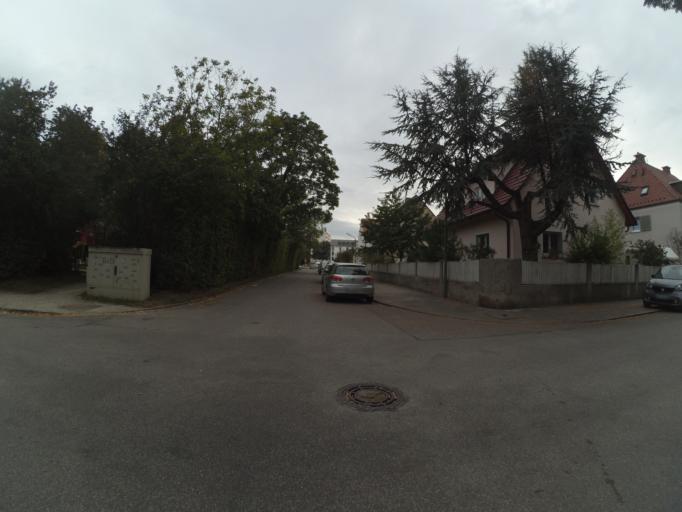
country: DE
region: Bavaria
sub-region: Upper Bavaria
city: Munich
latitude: 48.1809
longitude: 11.5252
